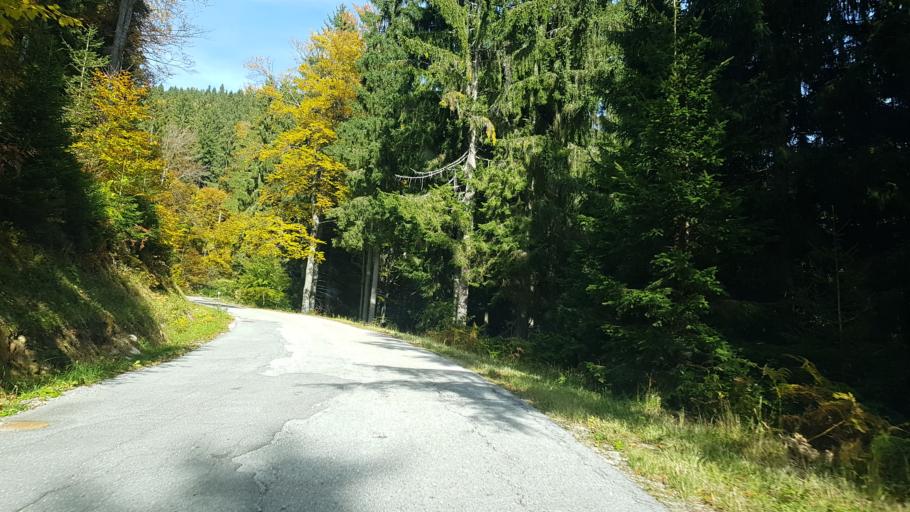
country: SI
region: Slovenj Gradec
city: Legen
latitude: 46.4950
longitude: 15.1860
